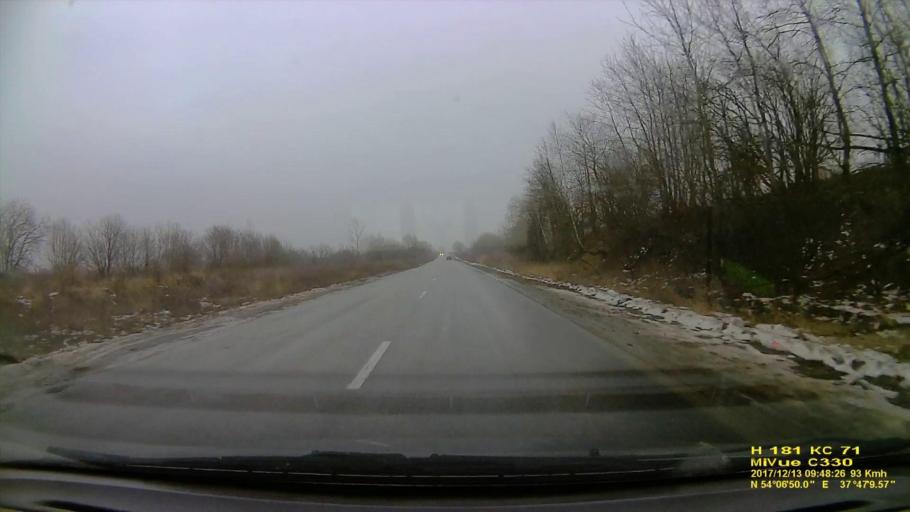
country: RU
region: Tula
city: Bolokhovo
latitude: 54.1139
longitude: 37.7862
